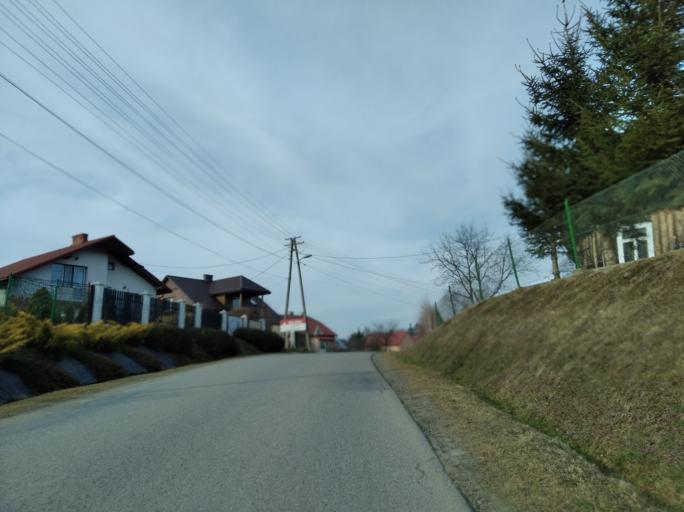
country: PL
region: Subcarpathian Voivodeship
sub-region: Powiat brzozowski
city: Turze Pole
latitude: 49.6696
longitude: 22.0030
